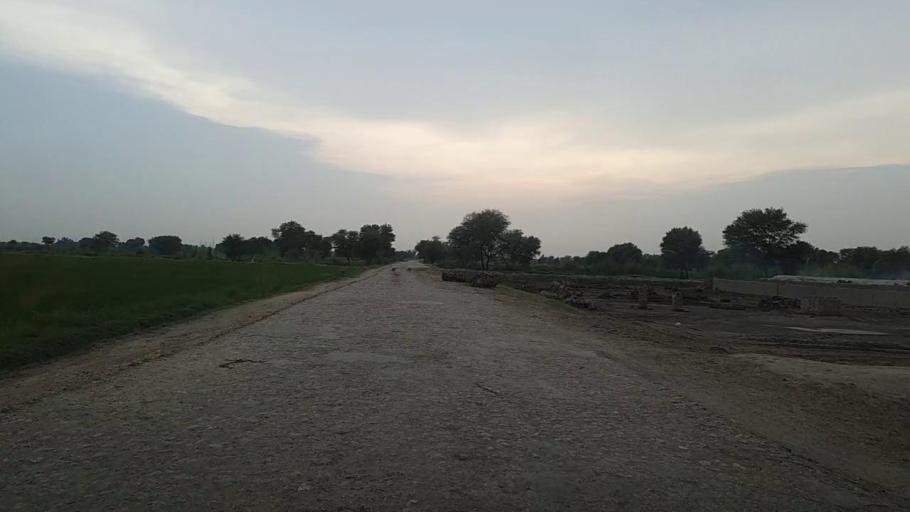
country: PK
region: Sindh
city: Khanpur
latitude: 27.8486
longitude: 69.4370
